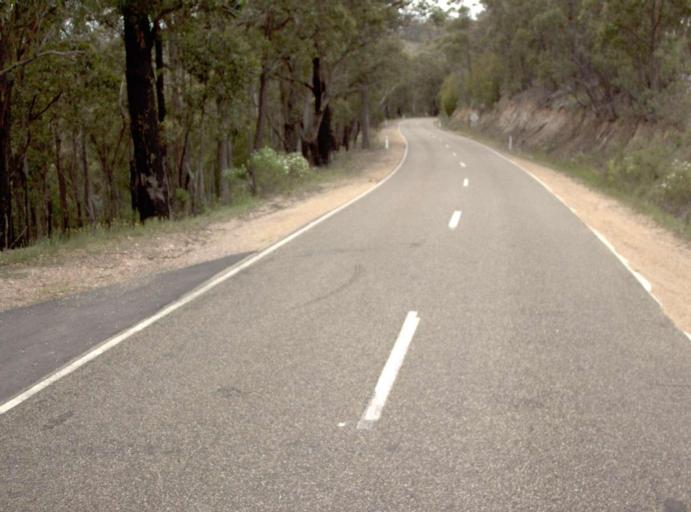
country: AU
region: Victoria
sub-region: East Gippsland
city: Bairnsdale
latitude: -37.6682
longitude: 147.2804
